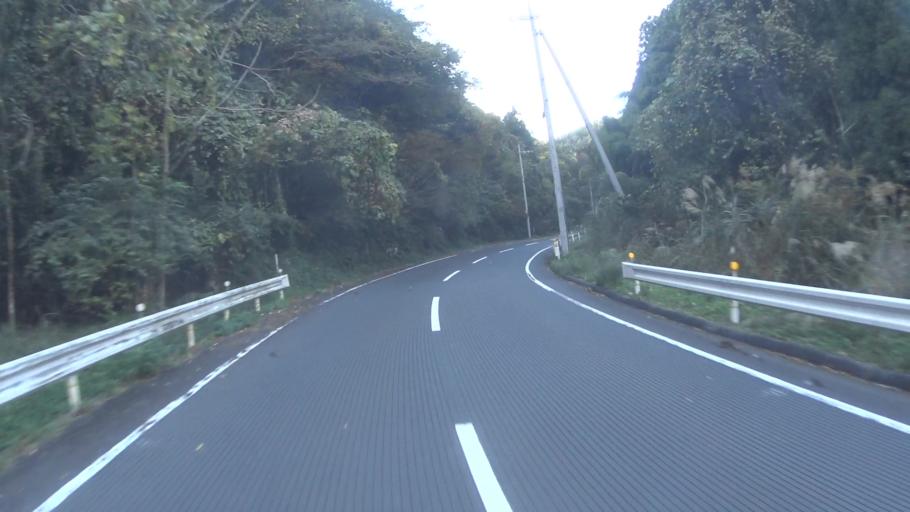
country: JP
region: Kyoto
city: Maizuru
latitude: 35.4604
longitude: 135.2541
